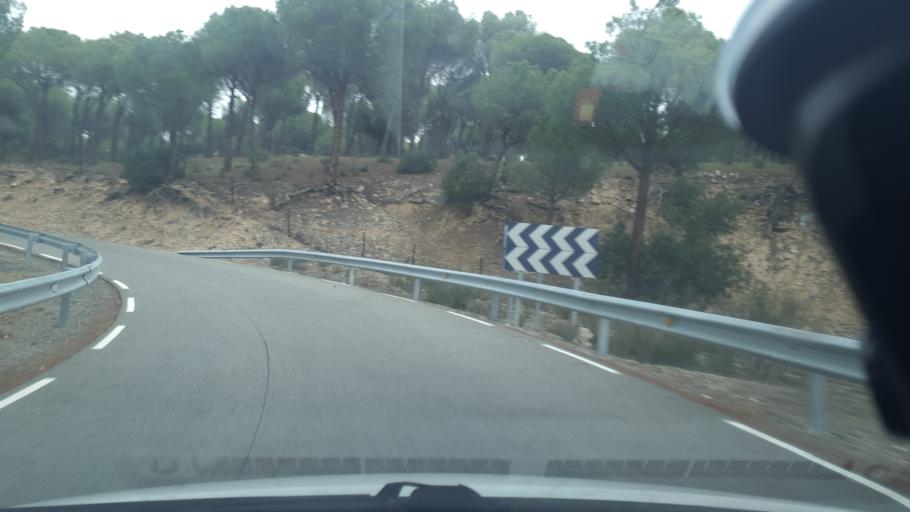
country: ES
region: Castille and Leon
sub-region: Provincia de Avila
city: Pozanco
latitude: 40.8256
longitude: -4.6877
